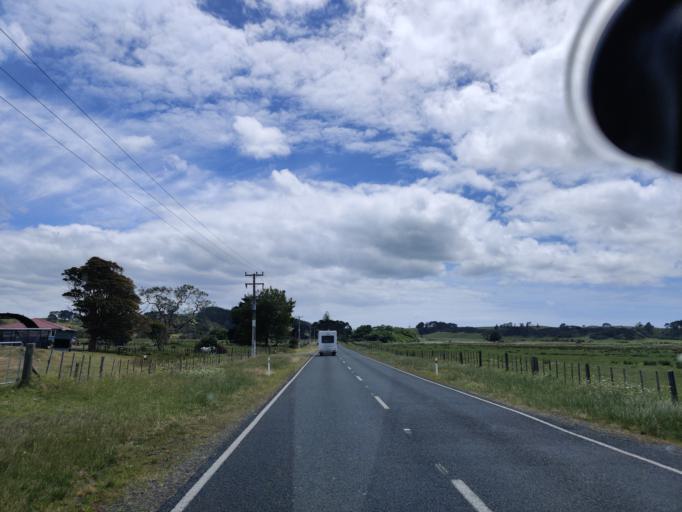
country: NZ
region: Northland
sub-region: Far North District
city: Kaitaia
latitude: -34.7640
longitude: 173.0762
